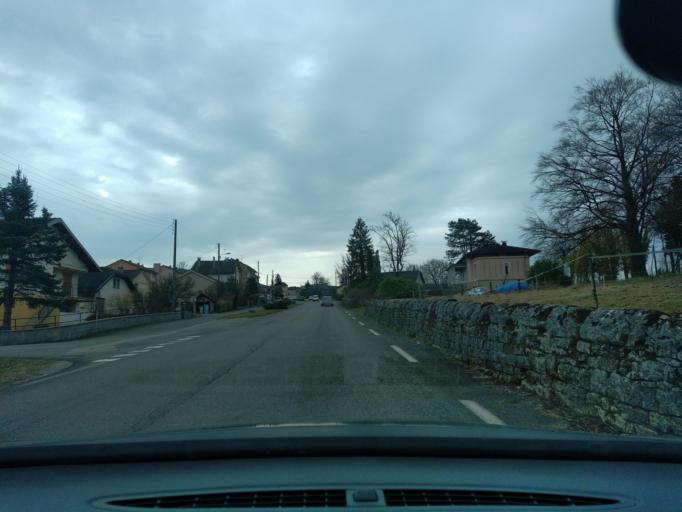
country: FR
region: Franche-Comte
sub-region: Departement du Jura
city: Arinthod
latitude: 46.3981
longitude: 5.5659
